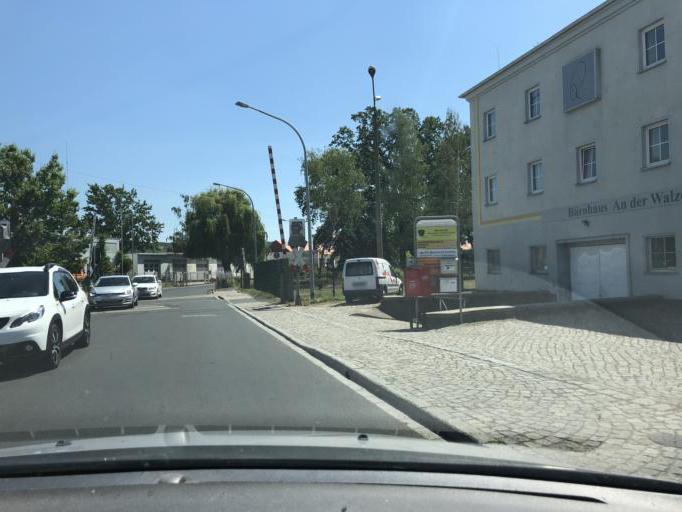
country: DE
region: Saxony
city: Coswig
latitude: 51.1196
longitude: 13.5851
